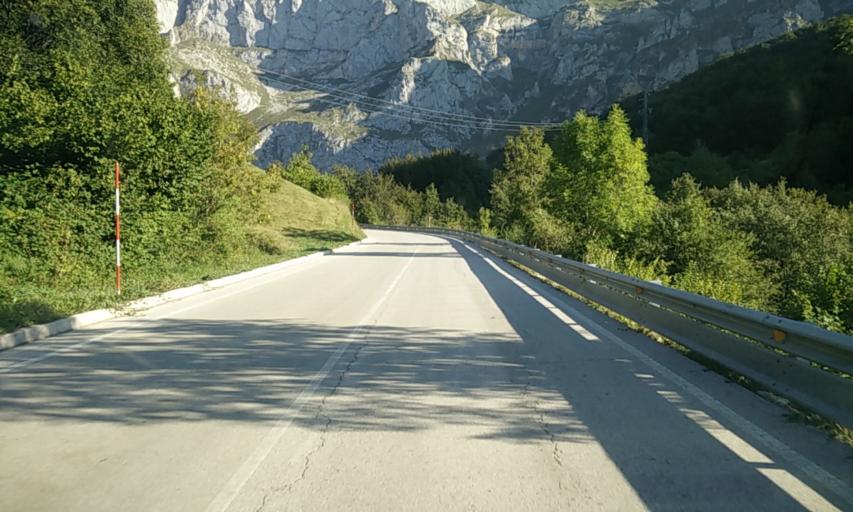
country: ES
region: Castille and Leon
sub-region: Provincia de Leon
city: Posada de Valdeon
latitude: 43.1394
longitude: -4.8096
